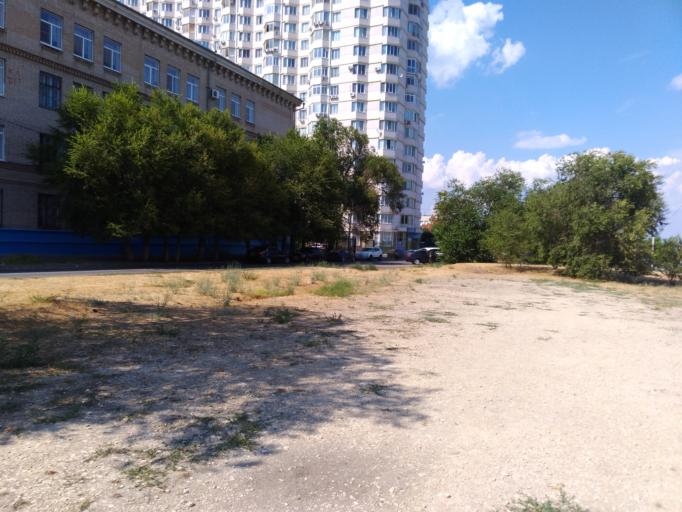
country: RU
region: Volgograd
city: Volgograd
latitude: 48.7182
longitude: 44.5370
